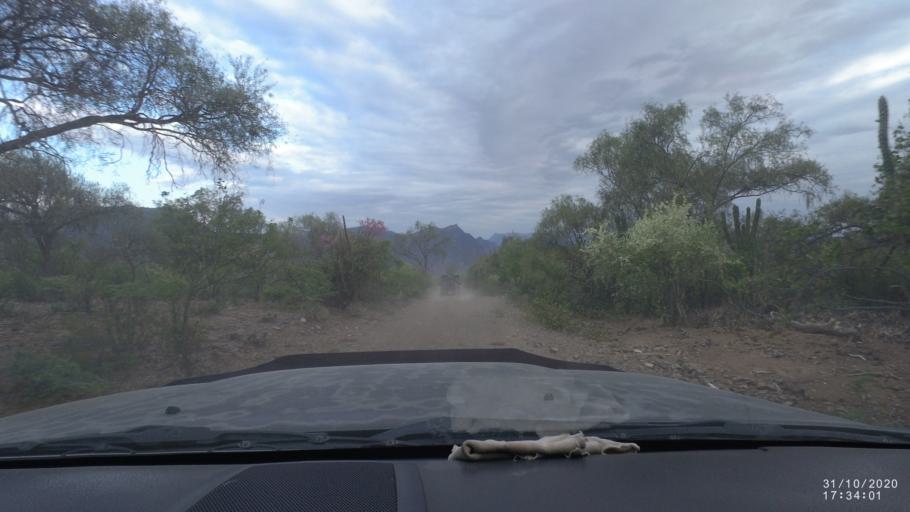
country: BO
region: Chuquisaca
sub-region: Provincia Zudanez
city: Mojocoya
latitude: -18.5997
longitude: -64.5490
